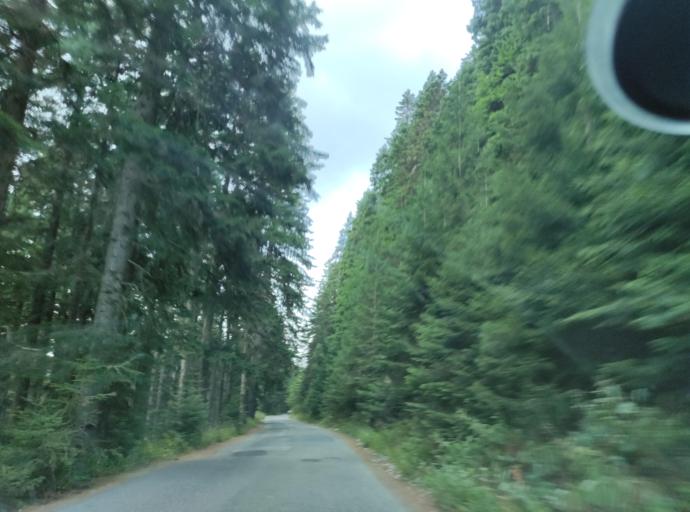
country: BG
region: Blagoevgrad
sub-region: Obshtina Bansko
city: Bansko
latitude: 41.7798
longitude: 23.4419
